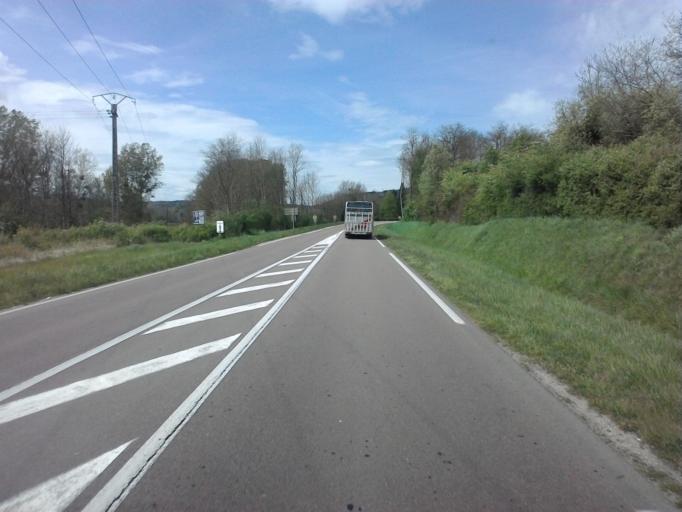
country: FR
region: Bourgogne
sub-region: Departement de l'Yonne
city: Vermenton
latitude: 47.6081
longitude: 3.7591
